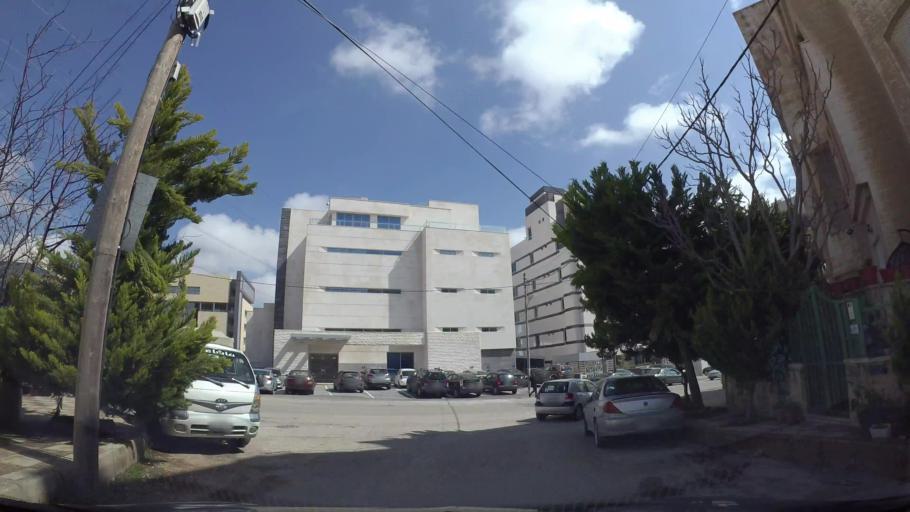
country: JO
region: Amman
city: Wadi as Sir
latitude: 31.9616
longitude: 35.8439
